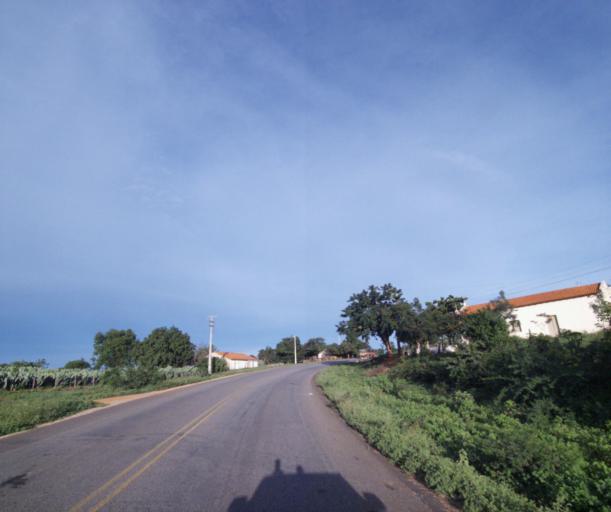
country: BR
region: Bahia
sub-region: Caetite
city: Caetite
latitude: -14.1717
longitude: -42.1875
